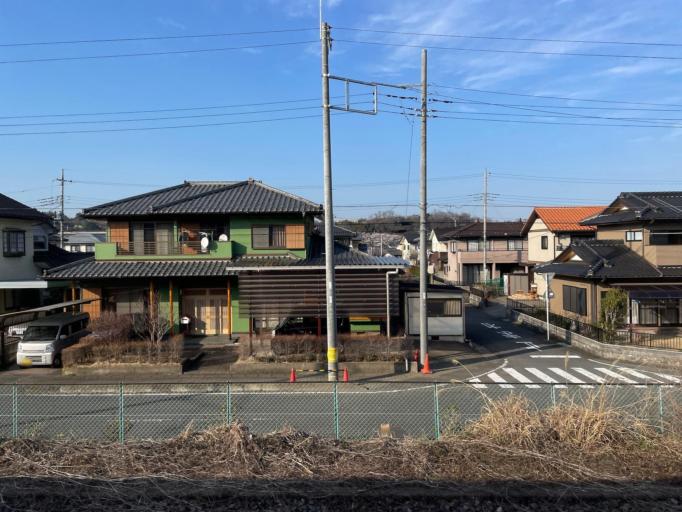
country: JP
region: Gunma
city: Annaka
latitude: 36.3054
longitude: 138.8055
